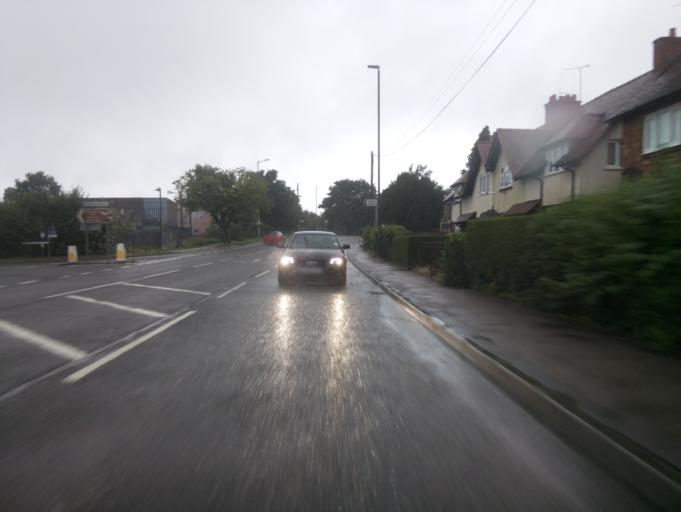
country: GB
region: England
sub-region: Gloucestershire
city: Tewkesbury
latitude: 51.9859
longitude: -2.1621
